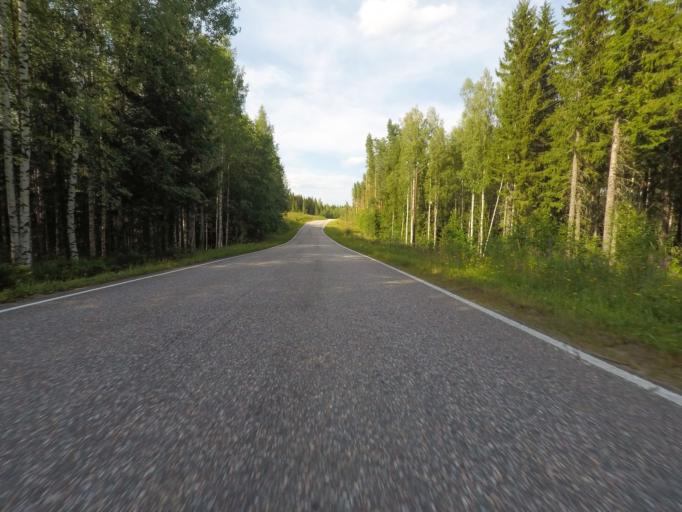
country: FI
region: Southern Savonia
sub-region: Savonlinna
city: Sulkava
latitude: 61.7743
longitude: 28.2391
